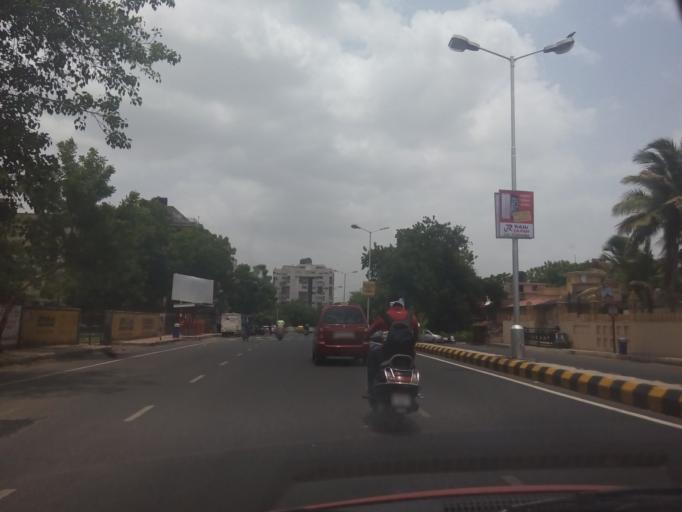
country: IN
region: Gujarat
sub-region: Ahmadabad
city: Sarkhej
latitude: 23.0430
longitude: 72.5226
